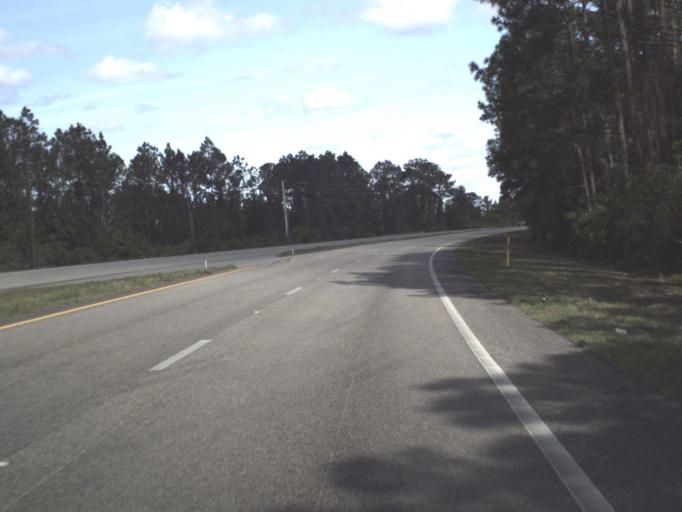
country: US
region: Florida
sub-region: Flagler County
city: Bunnell
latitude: 29.3832
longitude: -81.1871
